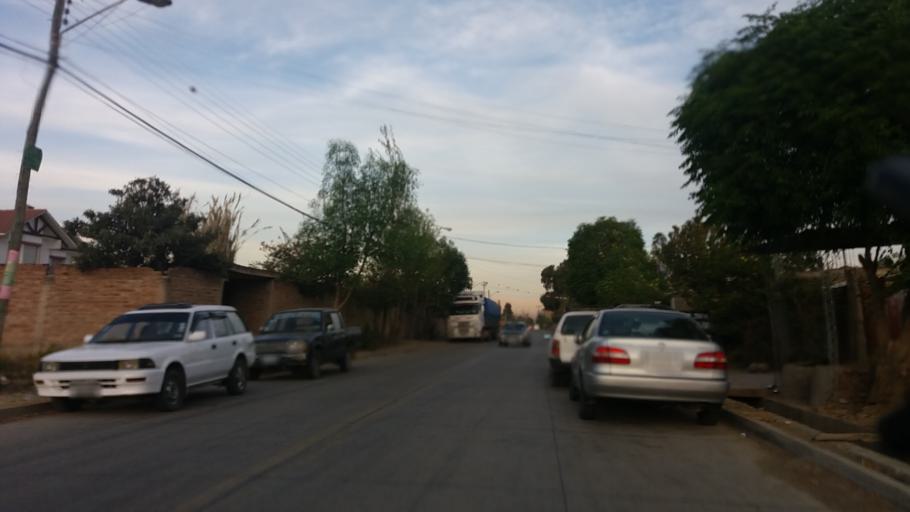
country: BO
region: Cochabamba
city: Cochabamba
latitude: -17.3677
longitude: -66.2127
